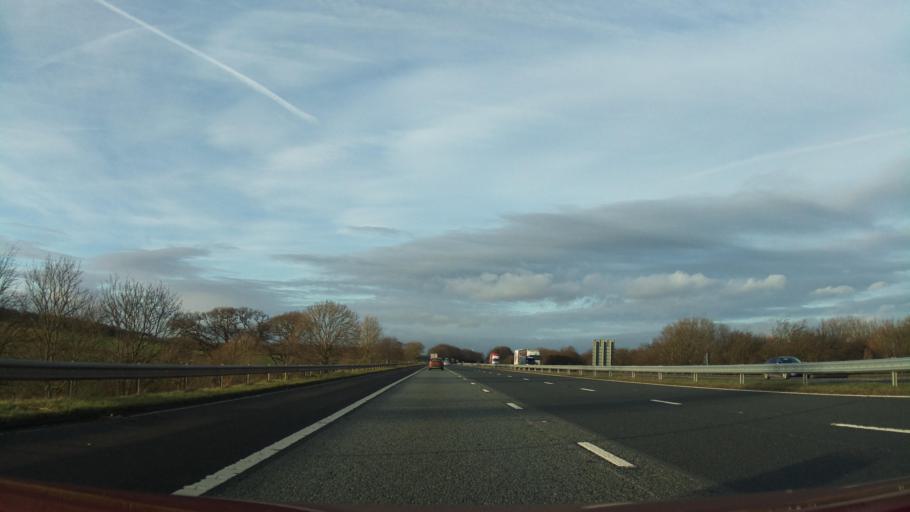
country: GB
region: England
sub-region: Cumbria
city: Scotby
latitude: 54.8091
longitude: -2.8772
